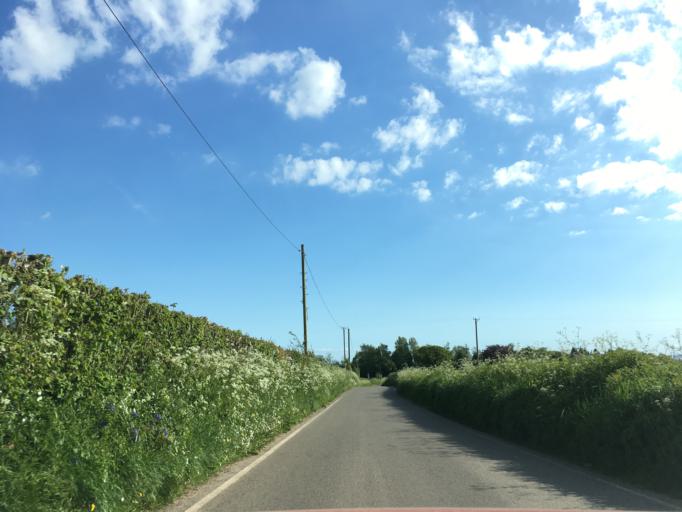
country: GB
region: Wales
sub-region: Newport
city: Marshfield
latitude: 51.5415
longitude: -3.1011
